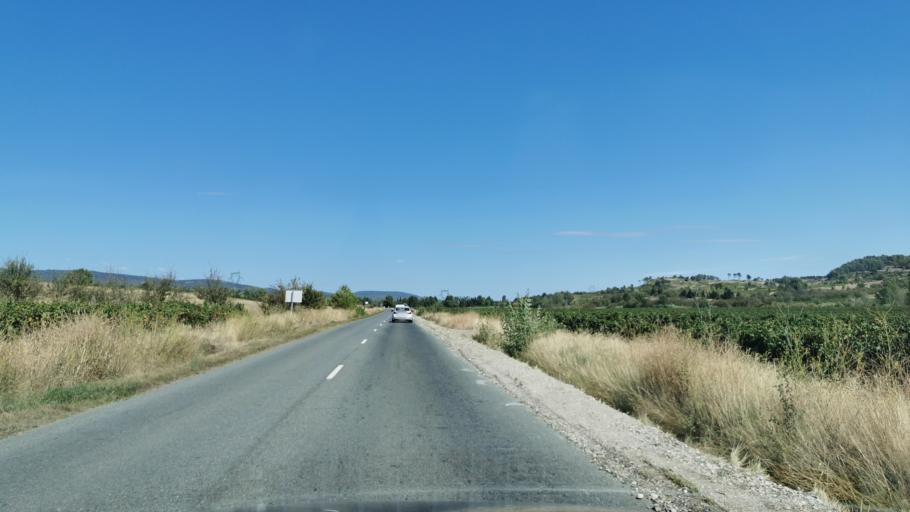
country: FR
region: Languedoc-Roussillon
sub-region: Departement de l'Aude
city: Conques-sur-Orbiel
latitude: 43.2955
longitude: 2.4548
